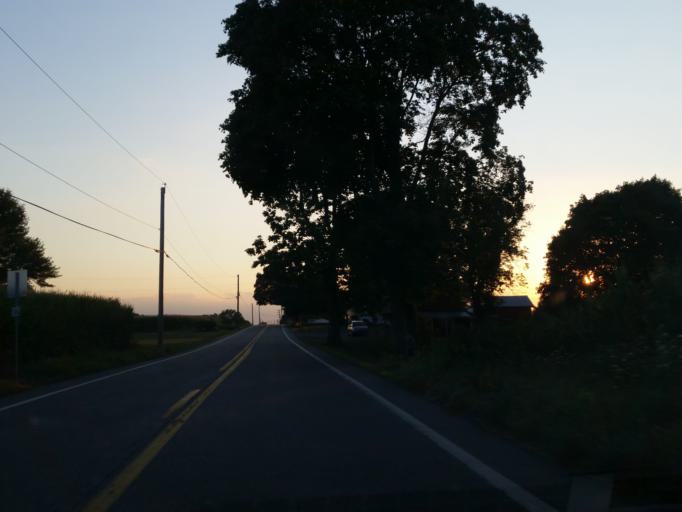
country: US
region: Pennsylvania
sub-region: Lebanon County
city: Cornwall
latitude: 40.2879
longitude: -76.3702
